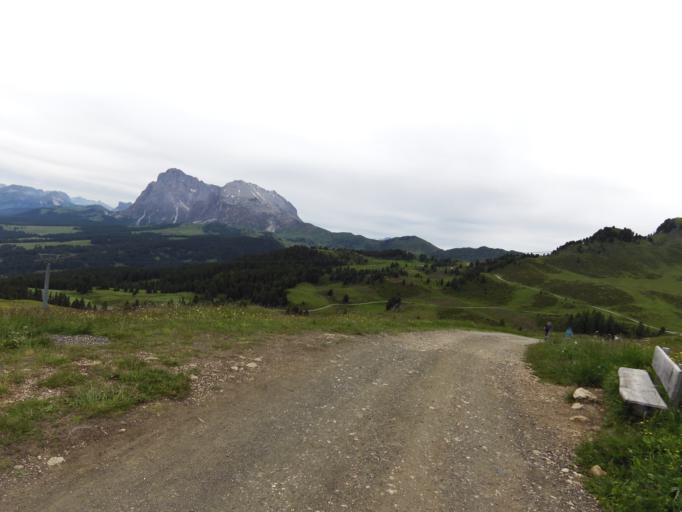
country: IT
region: Trentino-Alto Adige
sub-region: Bolzano
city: Ortisei
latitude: 46.5200
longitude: 11.6448
